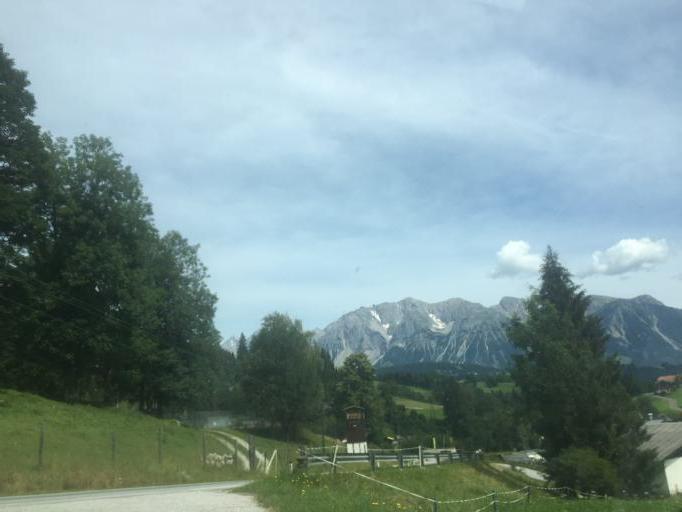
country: AT
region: Styria
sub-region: Politischer Bezirk Liezen
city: Schladming
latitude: 47.3700
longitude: 13.6766
